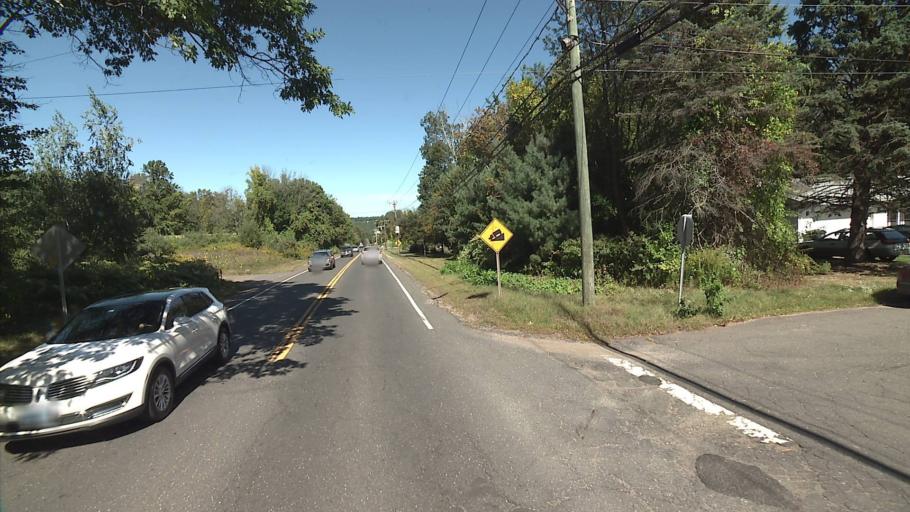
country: US
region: Connecticut
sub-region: New Haven County
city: Prospect
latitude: 41.4729
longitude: -72.9681
